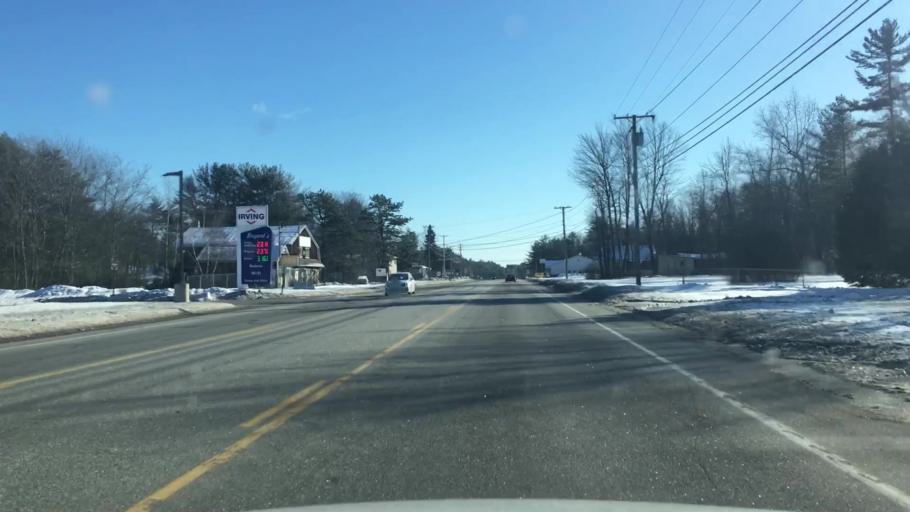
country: US
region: Maine
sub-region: Androscoggin County
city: Turner
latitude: 44.1885
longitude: -70.2376
